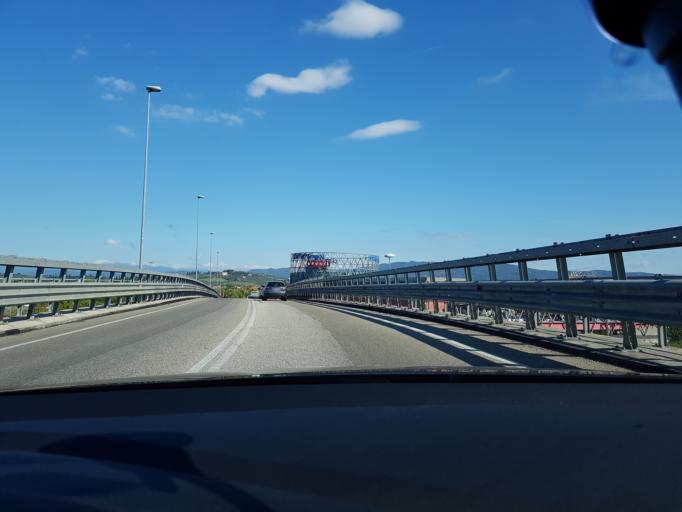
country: IT
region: Tuscany
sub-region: Province of Florence
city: Empoli
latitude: 43.7117
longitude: 10.9212
